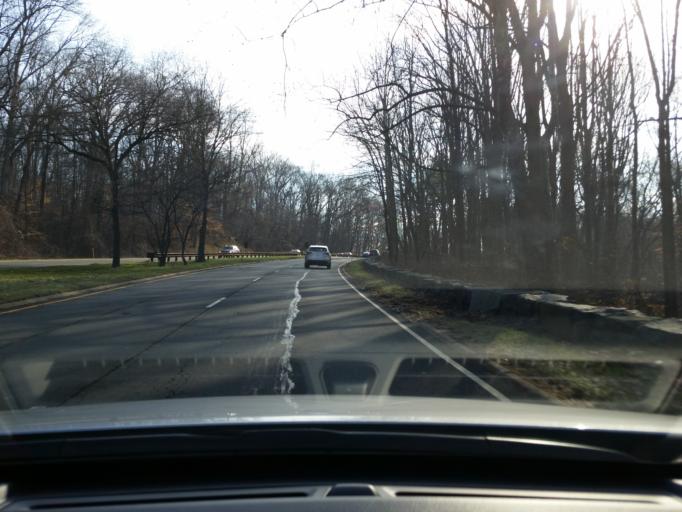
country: US
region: Maryland
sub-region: Montgomery County
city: Brookmont
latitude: 38.9334
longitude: -77.1289
